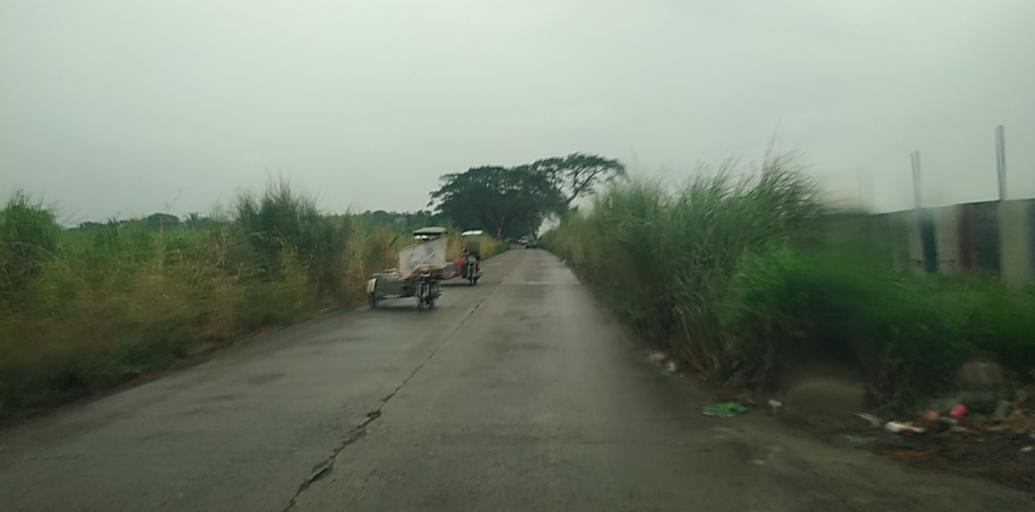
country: PH
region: Central Luzon
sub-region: Province of Pampanga
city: San Antonio
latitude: 15.1580
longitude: 120.6949
